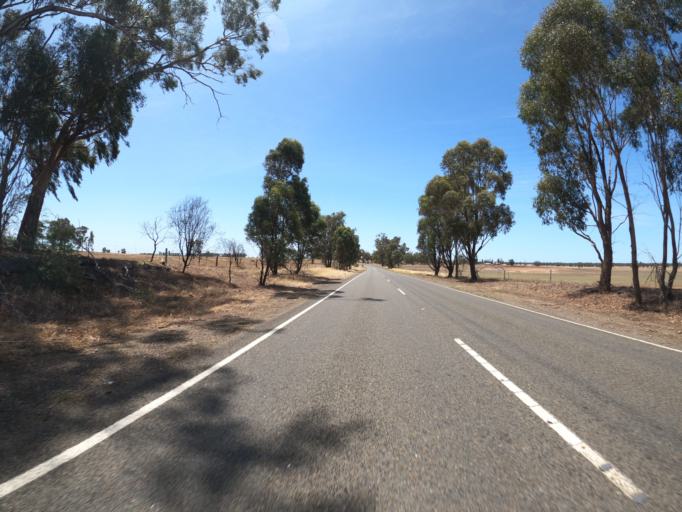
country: AU
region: Victoria
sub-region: Moira
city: Yarrawonga
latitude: -36.1012
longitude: 145.9931
